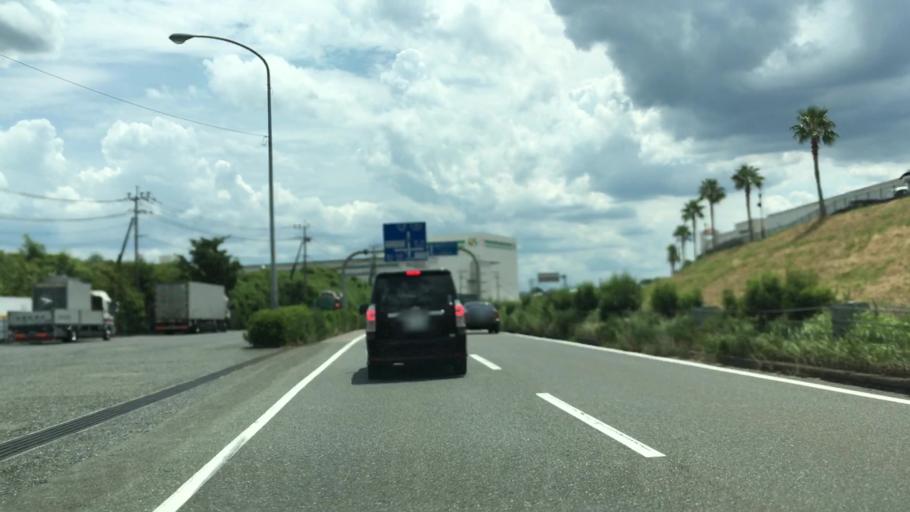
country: JP
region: Saga Prefecture
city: Tosu
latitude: 33.4068
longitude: 130.5128
